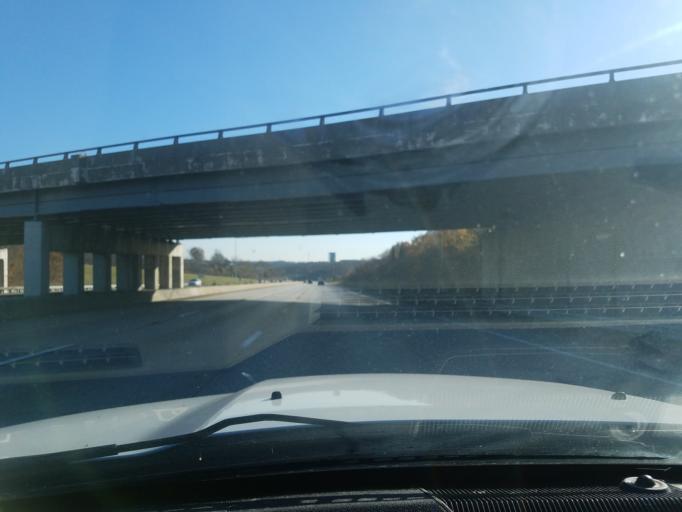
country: US
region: Kentucky
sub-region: Kenton County
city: Lakeside Park
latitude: 39.0262
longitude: -84.5701
